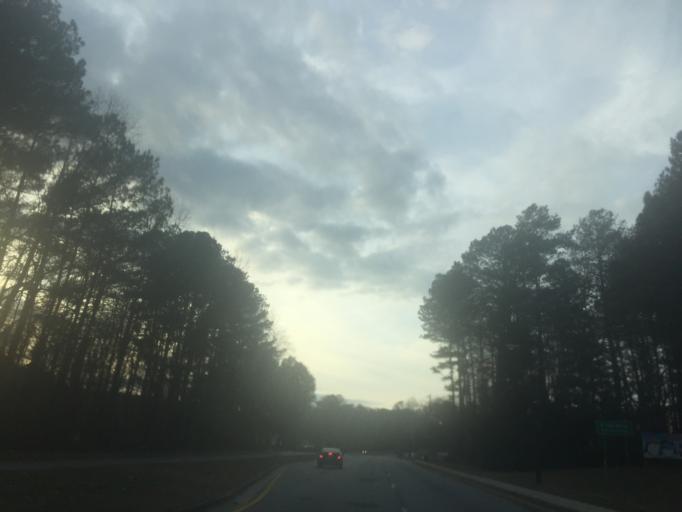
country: US
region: Georgia
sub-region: Clayton County
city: Riverdale
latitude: 33.5945
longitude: -84.4111
